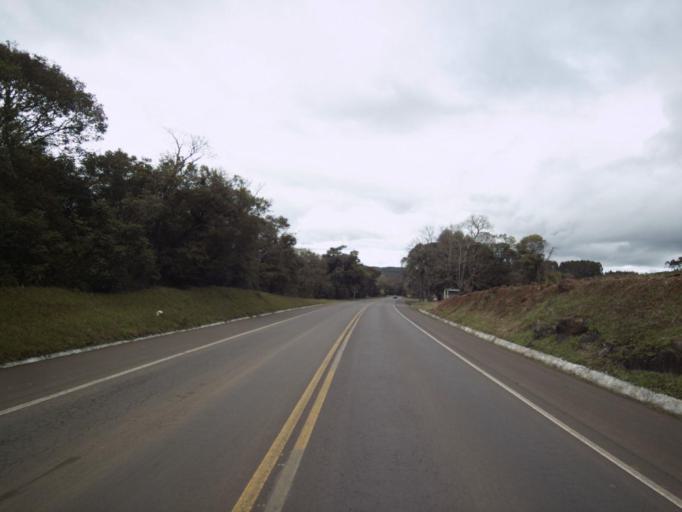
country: BR
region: Santa Catarina
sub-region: Concordia
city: Concordia
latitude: -27.2667
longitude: -51.9607
